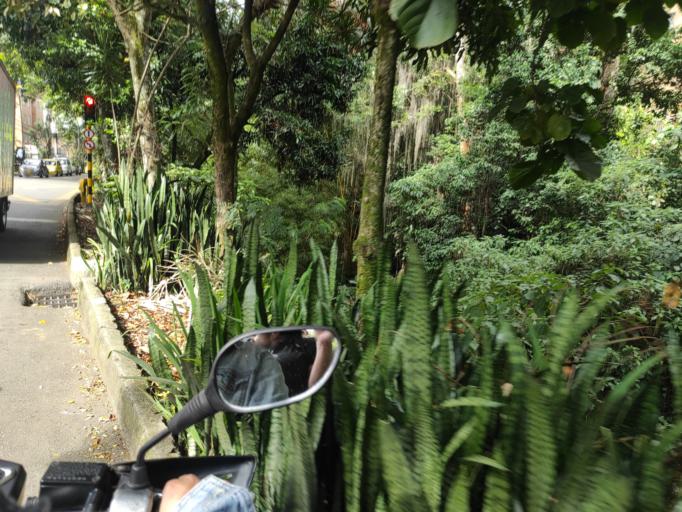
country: CO
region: Antioquia
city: Envigado
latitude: 6.1637
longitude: -75.5808
